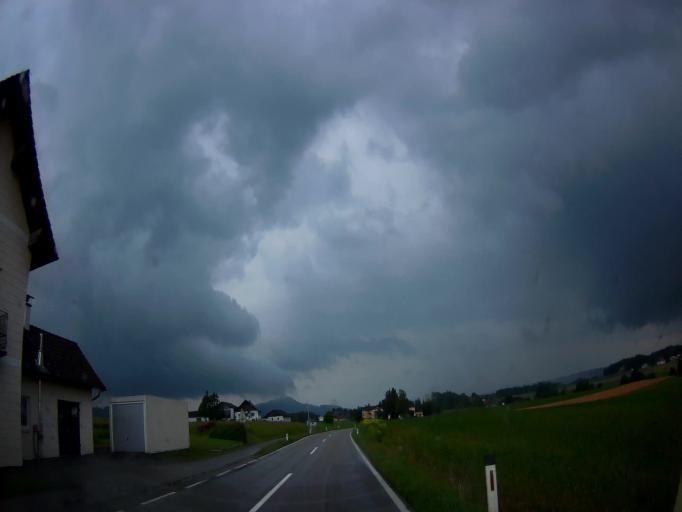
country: AT
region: Salzburg
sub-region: Politischer Bezirk Salzburg-Umgebung
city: Mattsee
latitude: 48.0041
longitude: 13.1237
